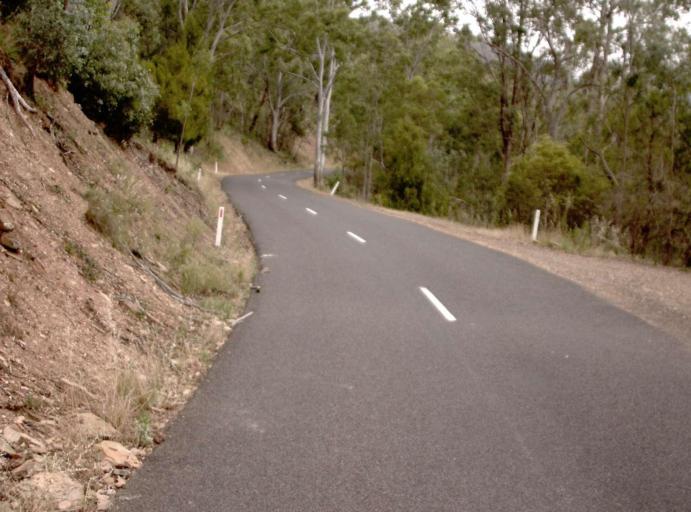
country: AU
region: Victoria
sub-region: Wellington
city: Heyfield
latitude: -37.8078
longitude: 146.6716
